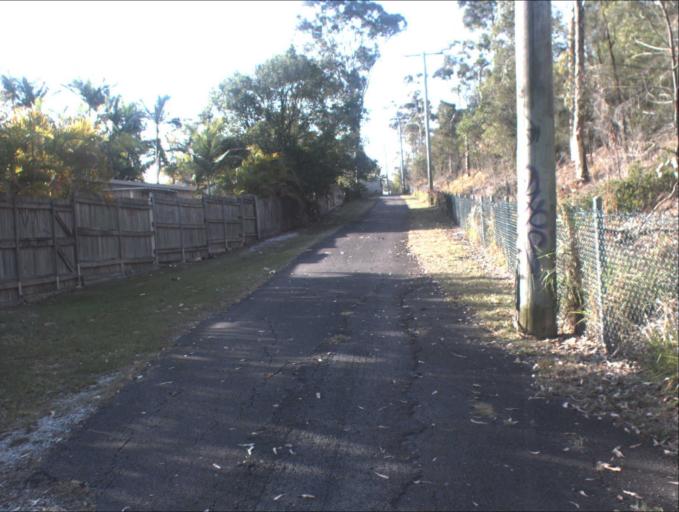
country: AU
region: Queensland
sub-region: Logan
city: Beenleigh
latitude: -27.6784
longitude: 153.1851
